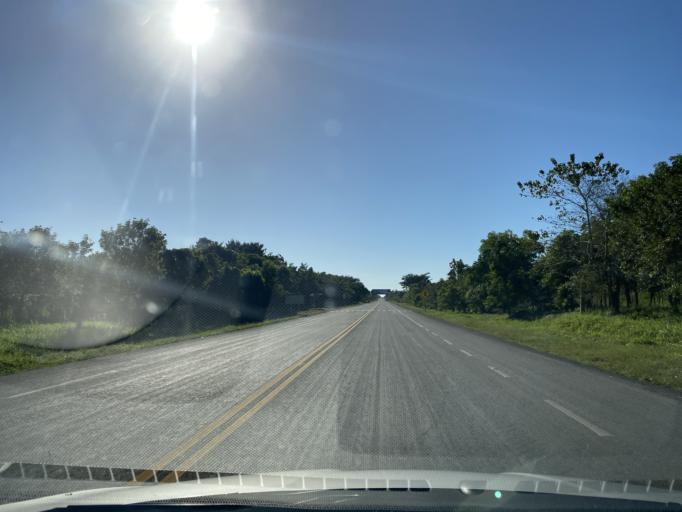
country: DO
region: Santo Domingo
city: Guerra
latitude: 18.5242
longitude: -69.7482
